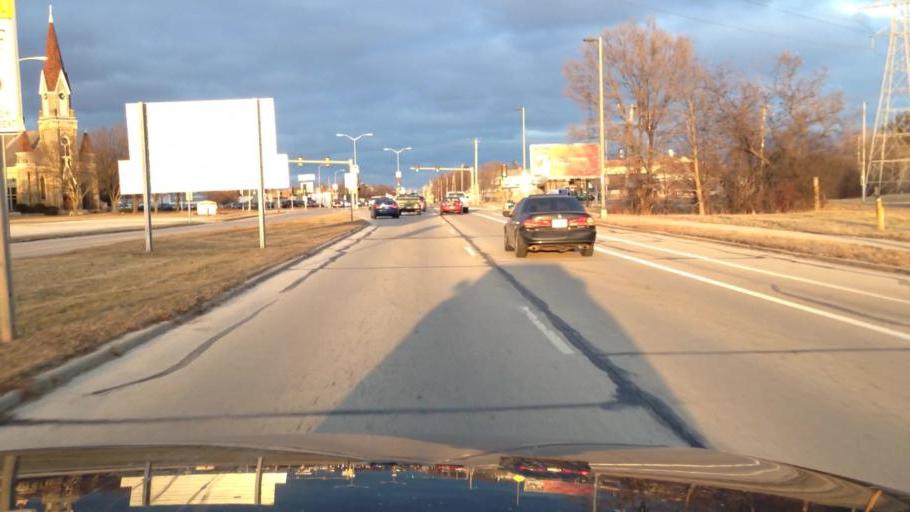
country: US
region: Wisconsin
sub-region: Milwaukee County
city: Greenfield
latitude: 42.9696
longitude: -87.9994
